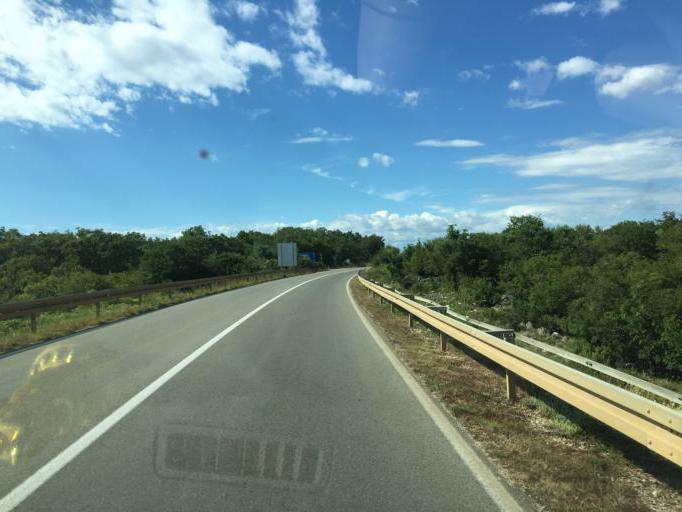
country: HR
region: Primorsko-Goranska
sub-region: Grad Krk
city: Krk
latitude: 45.0440
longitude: 14.5685
